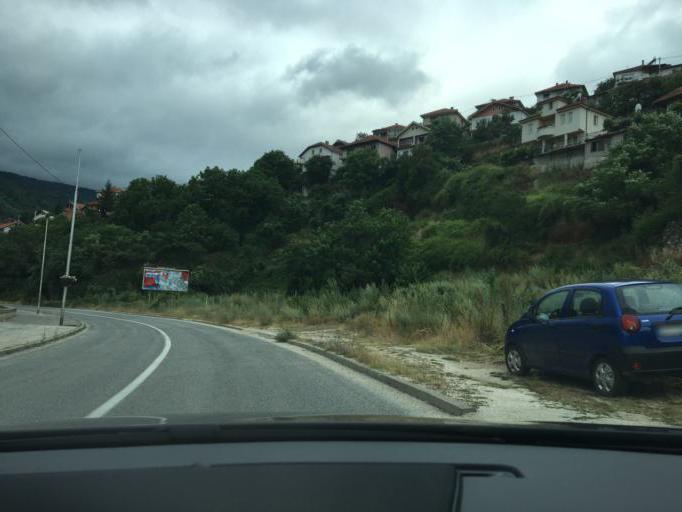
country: MK
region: Kriva Palanka
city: Kriva Palanka
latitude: 42.2052
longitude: 22.3332
